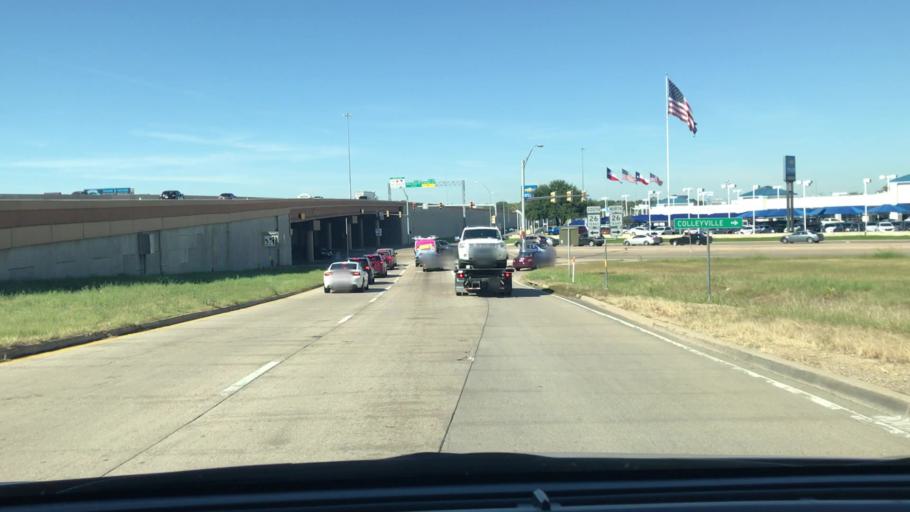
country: US
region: Texas
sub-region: Tarrant County
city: North Richland Hills
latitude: 32.8333
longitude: -97.2139
